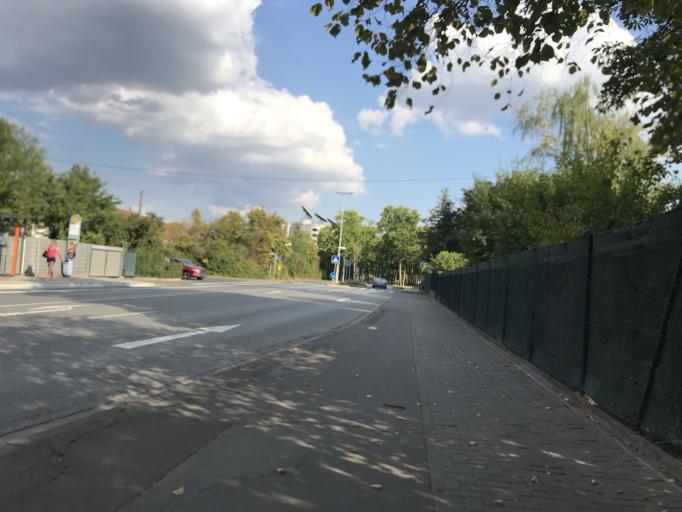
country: DE
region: Rheinland-Pfalz
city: Mainz
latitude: 50.0164
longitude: 8.2936
